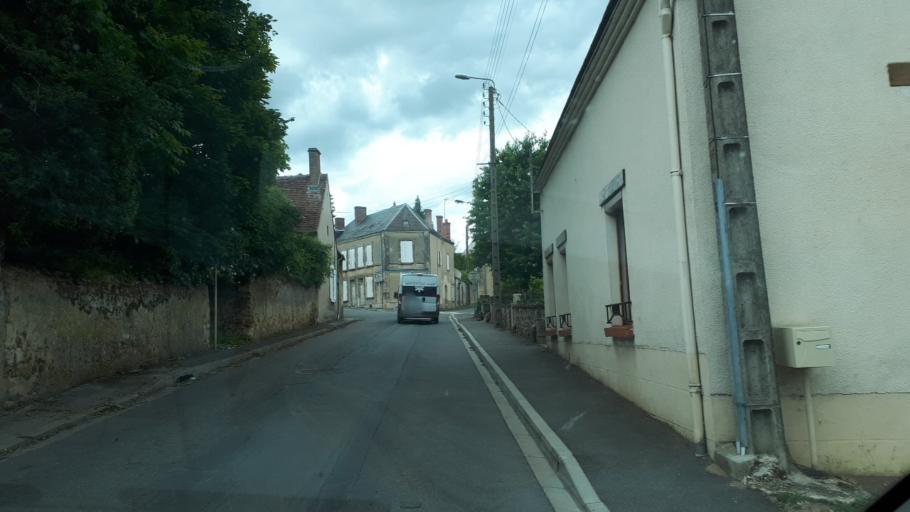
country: FR
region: Centre
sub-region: Departement du Cher
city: Gracay
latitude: 47.1456
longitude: 1.8459
